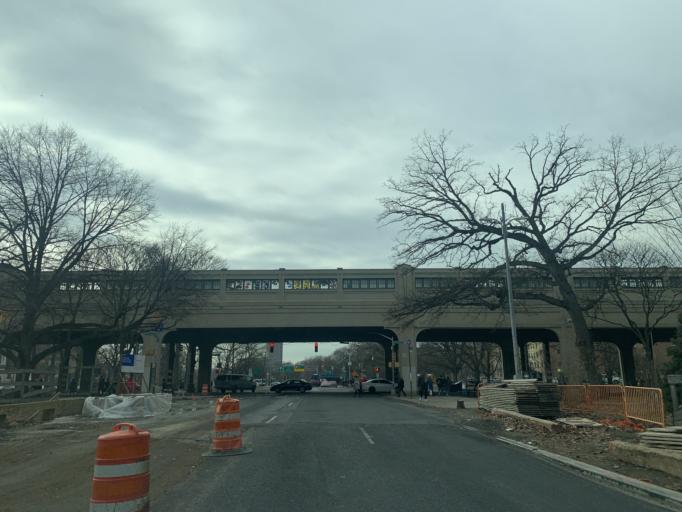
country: US
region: New York
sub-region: Bronx
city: The Bronx
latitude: 40.8573
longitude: -73.8669
